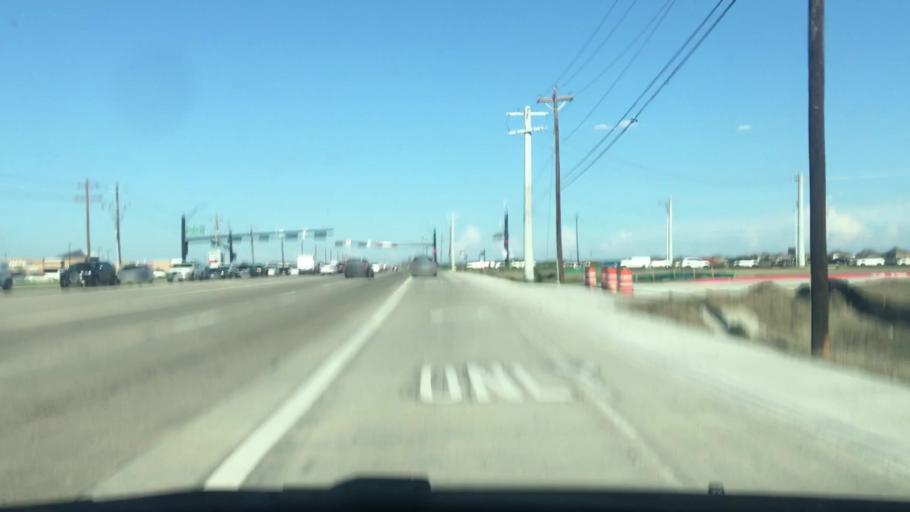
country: US
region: Texas
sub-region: Denton County
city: Little Elm
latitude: 33.2190
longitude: -96.8818
